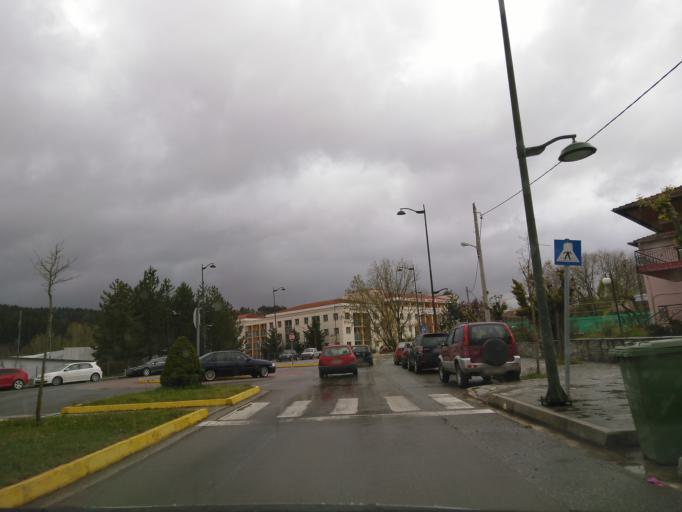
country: GR
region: West Macedonia
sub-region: Nomos Grevenon
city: Grevena
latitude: 40.0863
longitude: 21.4390
